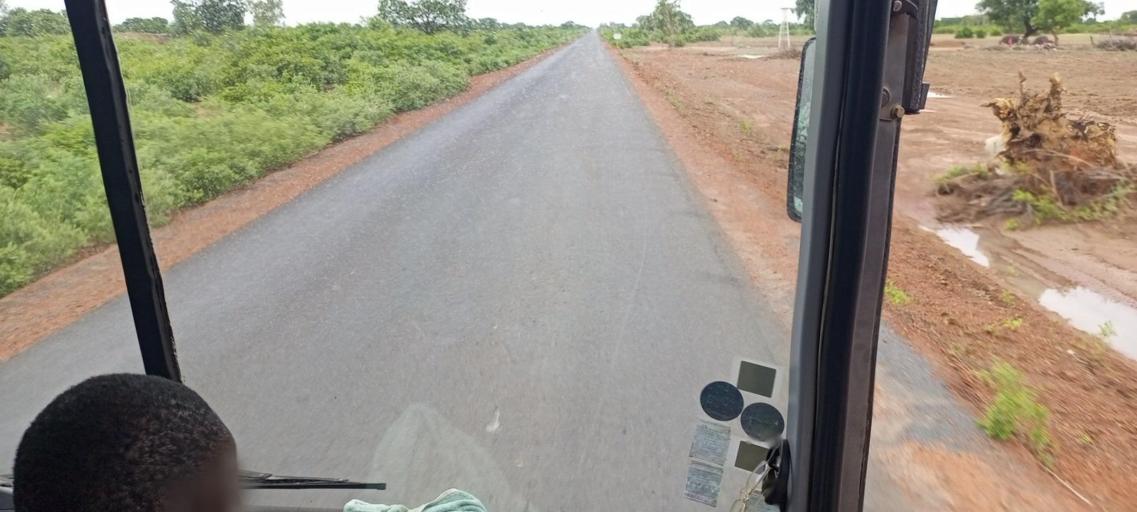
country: ML
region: Sikasso
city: Koutiala
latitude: 12.5674
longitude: -5.5989
